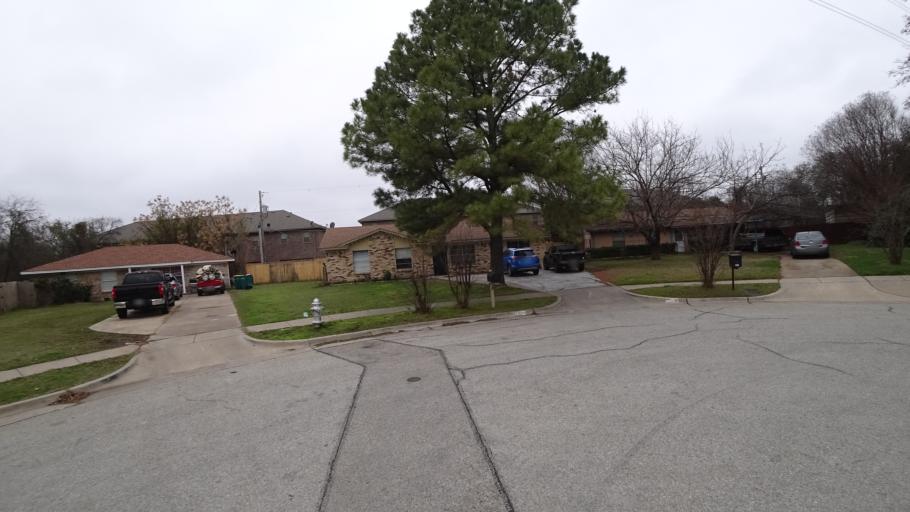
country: US
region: Texas
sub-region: Denton County
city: Lewisville
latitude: 33.0613
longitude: -97.0094
